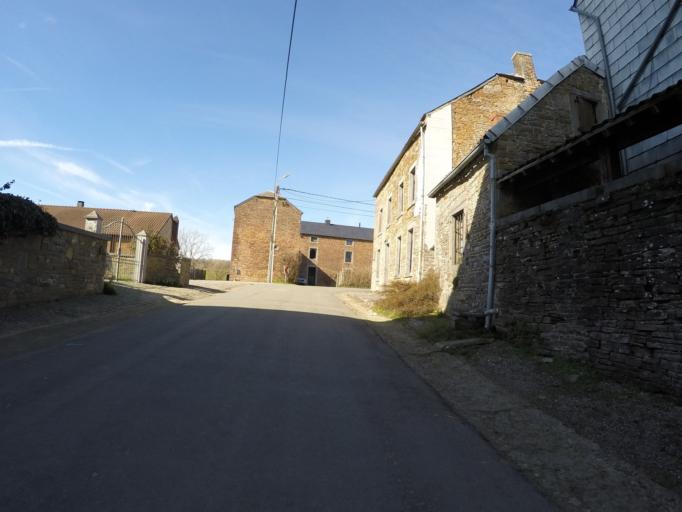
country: BE
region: Wallonia
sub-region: Province de Namur
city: Hamois
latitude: 50.3841
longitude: 5.1498
